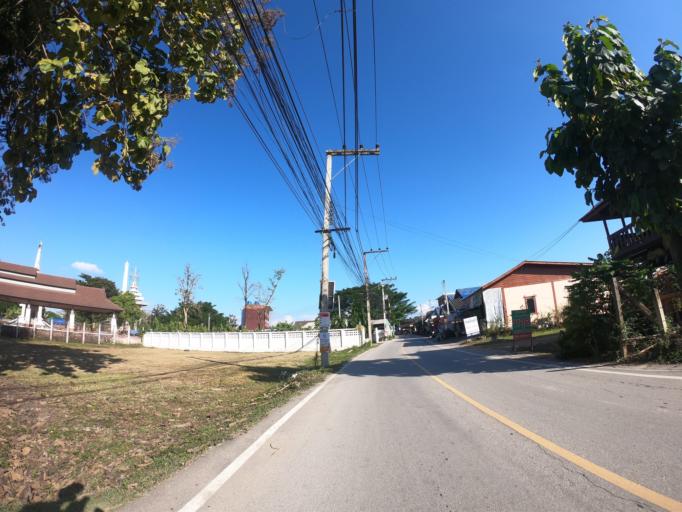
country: TH
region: Chiang Mai
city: San Sai
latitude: 18.8314
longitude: 99.0371
